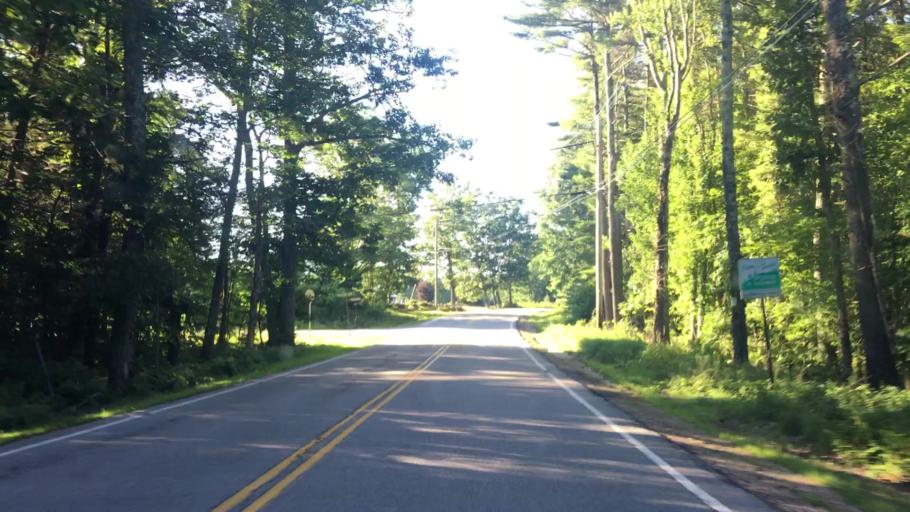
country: US
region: New Hampshire
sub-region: Rockingham County
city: Sandown
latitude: 42.9452
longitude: -71.1951
